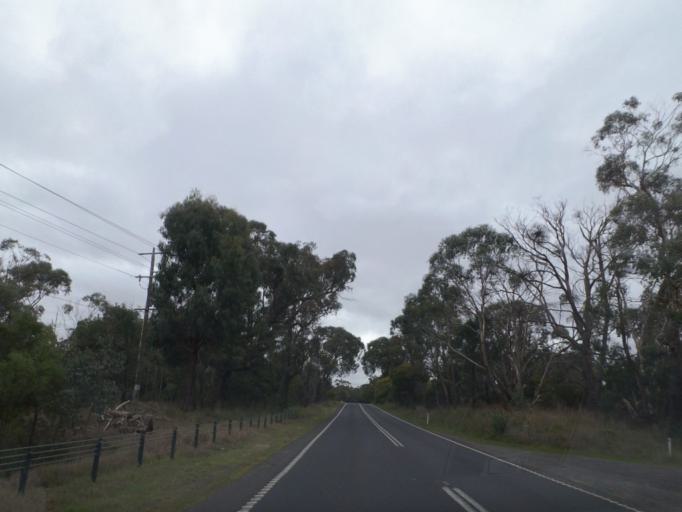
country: AU
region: Victoria
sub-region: Whittlesea
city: Whittlesea
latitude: -37.3829
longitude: 145.0298
